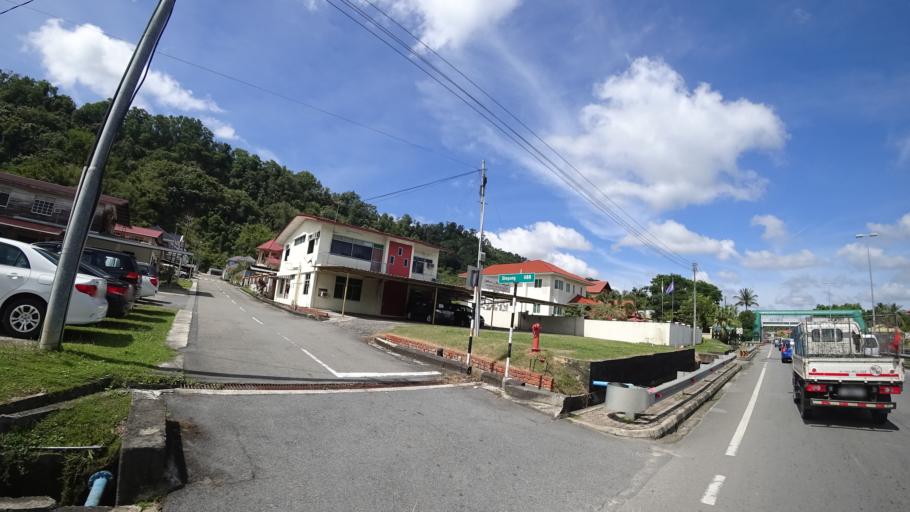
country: BN
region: Brunei and Muara
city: Bandar Seri Begawan
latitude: 4.8535
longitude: 114.8871
